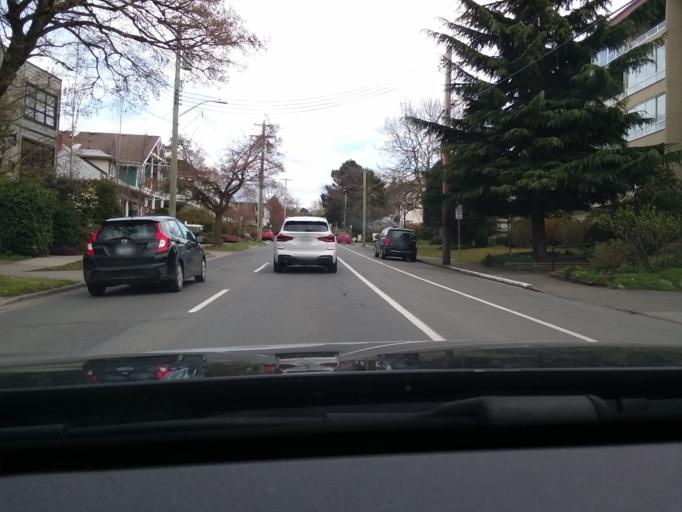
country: CA
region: British Columbia
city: Victoria
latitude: 48.4256
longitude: -123.3497
